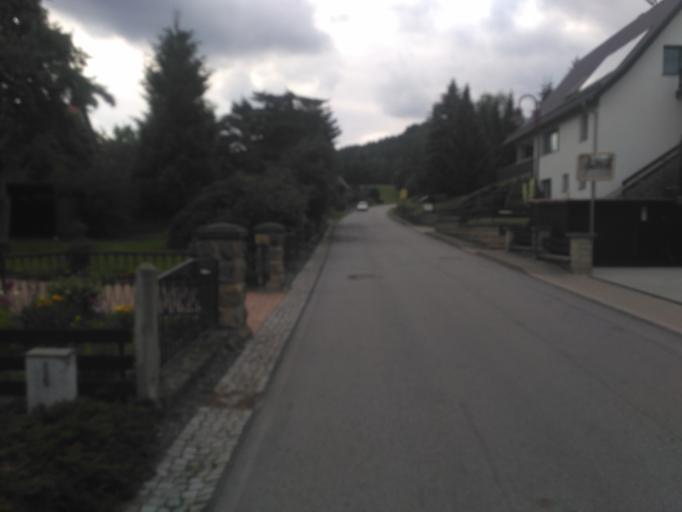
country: DE
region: Saxony
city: Kurort Gohrisch
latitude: 50.8976
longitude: 14.1213
